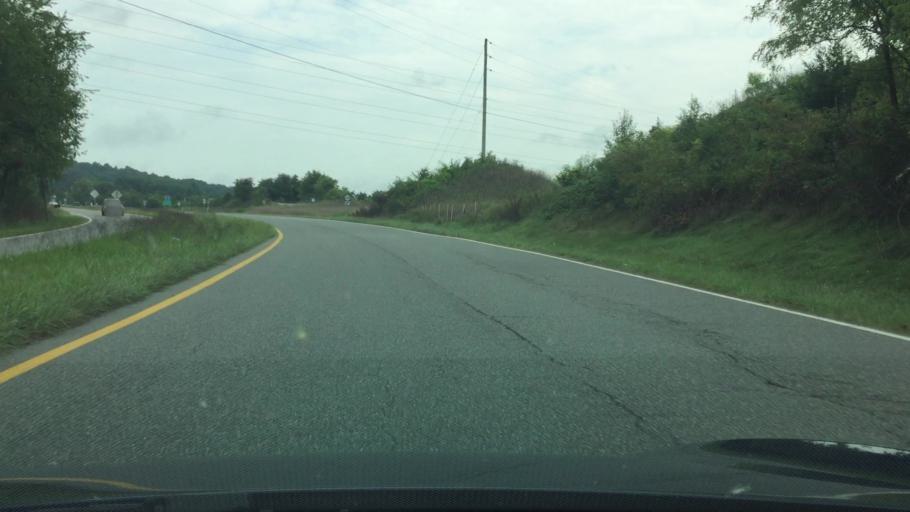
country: US
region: Virginia
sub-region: City of Radford
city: Radford
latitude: 37.0917
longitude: -80.5064
